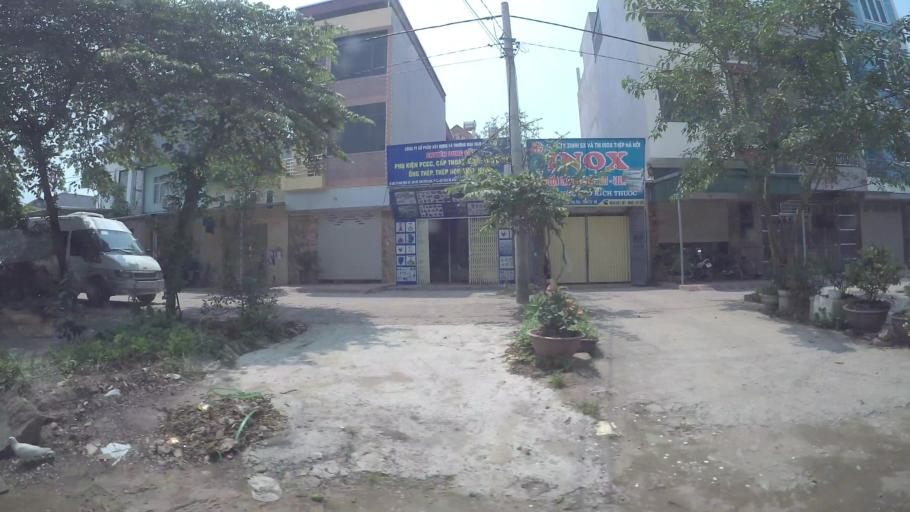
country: VN
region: Ha Noi
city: Van Dien
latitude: 20.9499
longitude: 105.8250
